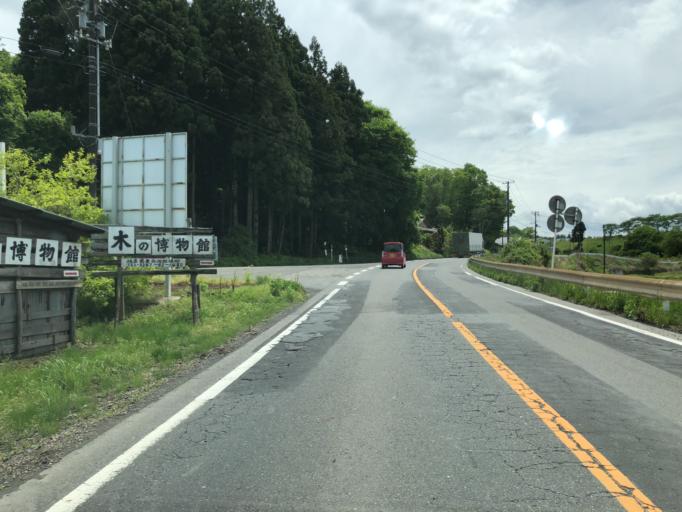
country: JP
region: Fukushima
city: Ishikawa
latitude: 37.0825
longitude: 140.3585
